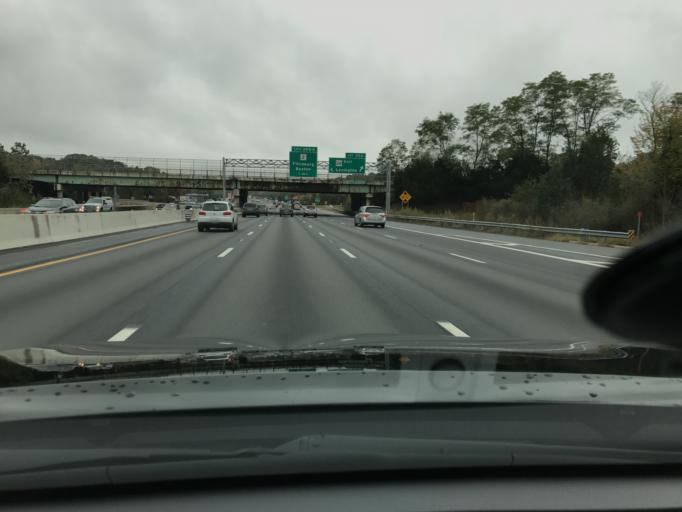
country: US
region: Massachusetts
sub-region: Middlesex County
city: Lexington
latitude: 42.4447
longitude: -71.2568
